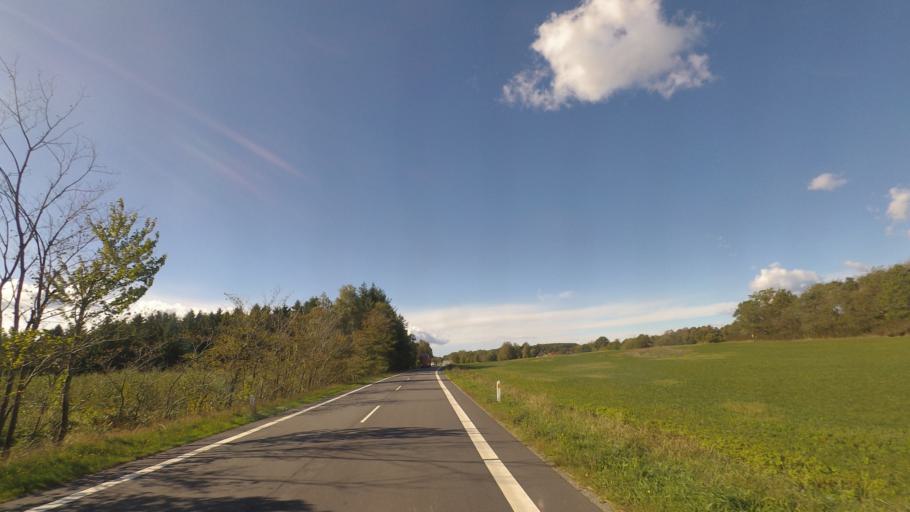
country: DK
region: Capital Region
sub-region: Bornholm Kommune
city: Akirkeby
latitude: 55.0660
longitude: 15.0073
